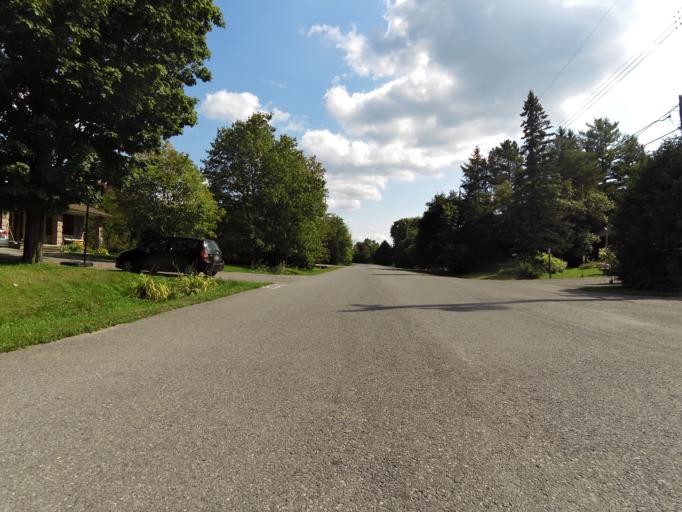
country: CA
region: Ontario
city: Bells Corners
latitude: 45.2332
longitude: -75.6942
